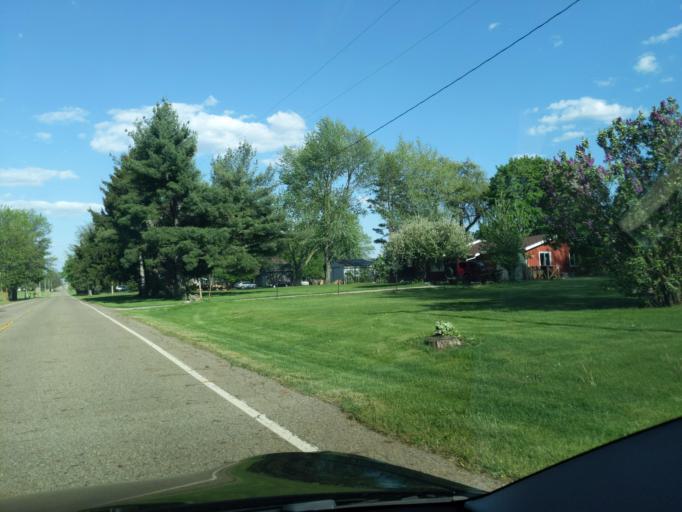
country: US
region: Michigan
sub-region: Eaton County
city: Dimondale
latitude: 42.6829
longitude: -84.6943
